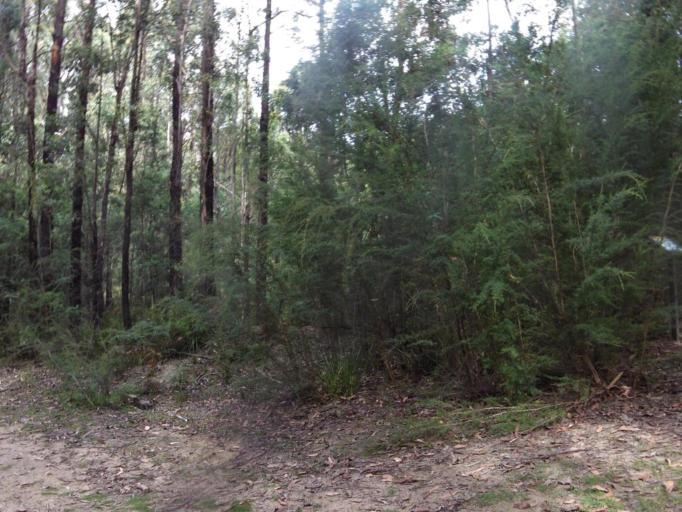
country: AU
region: Victoria
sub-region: Murrindindi
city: Alexandra
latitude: -37.3996
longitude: 145.5783
